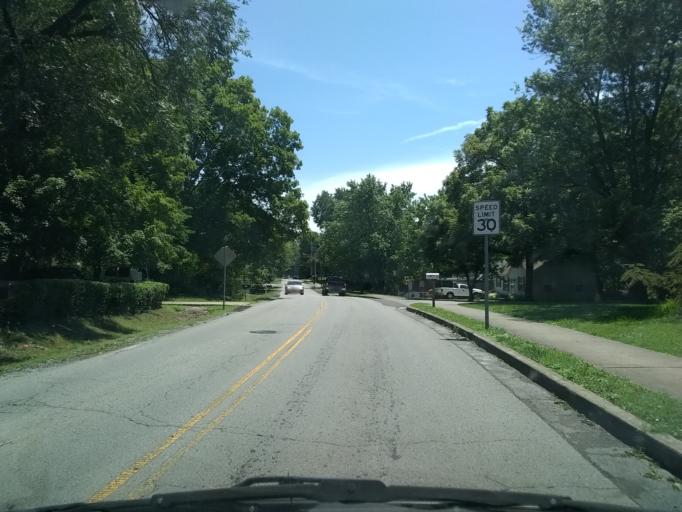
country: US
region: Tennessee
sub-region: Davidson County
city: Oak Hill
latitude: 36.1269
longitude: -86.7006
